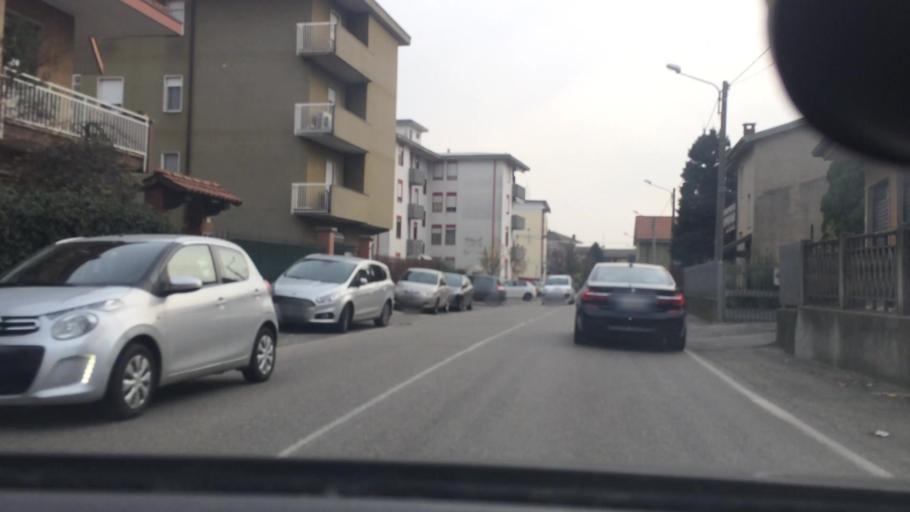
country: IT
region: Lombardy
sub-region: Provincia di Monza e Brianza
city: Cogliate
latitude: 45.6421
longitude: 9.0803
